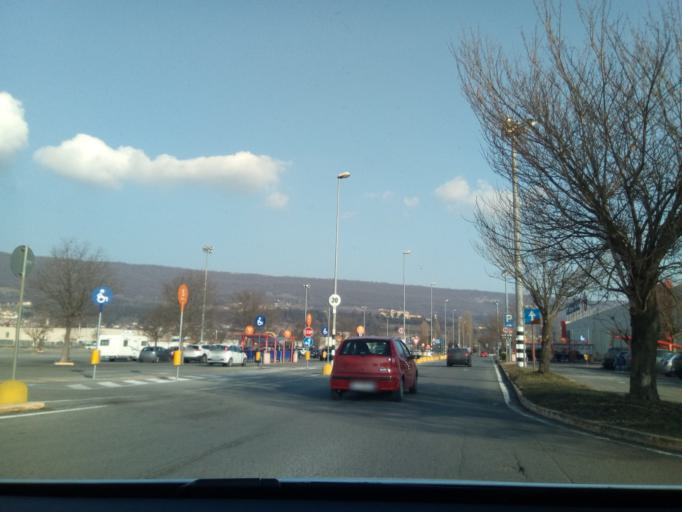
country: IT
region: Piedmont
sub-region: Provincia di Torino
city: Burolo
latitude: 45.4689
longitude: 7.9222
